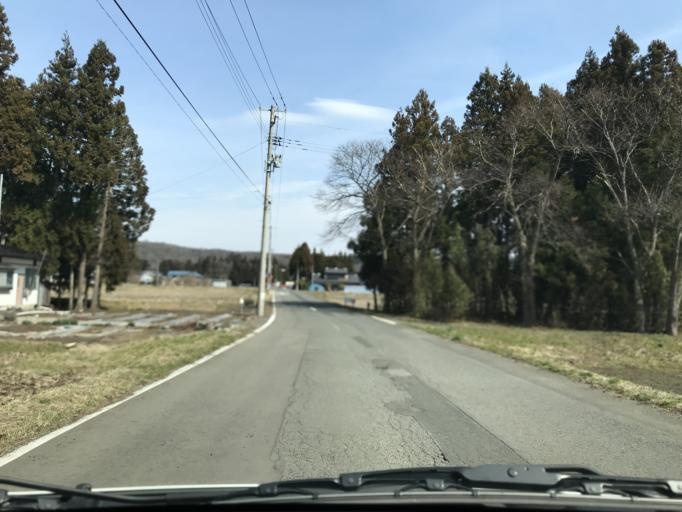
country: JP
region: Iwate
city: Mizusawa
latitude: 39.1206
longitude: 141.0137
